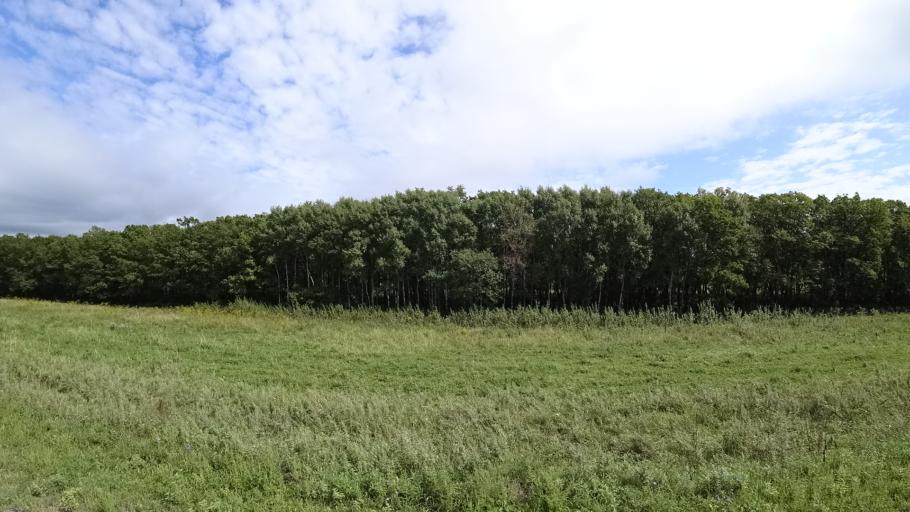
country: RU
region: Primorskiy
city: Lyalichi
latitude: 44.1444
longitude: 132.3896
